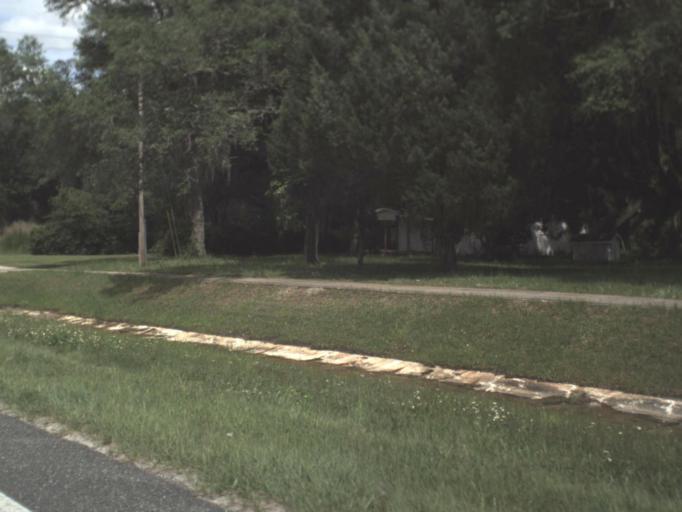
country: US
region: Florida
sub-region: Clay County
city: Middleburg
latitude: 30.0546
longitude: -81.8836
